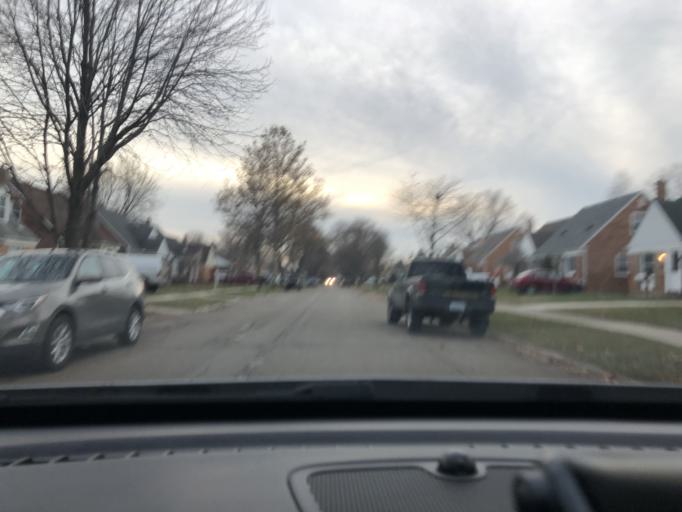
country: US
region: Michigan
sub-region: Wayne County
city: Allen Park
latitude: 42.2882
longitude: -83.2187
